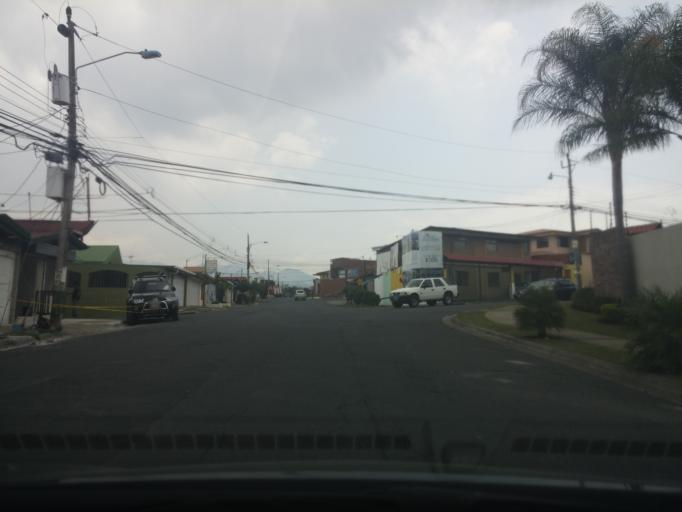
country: CR
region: Heredia
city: San Pablo
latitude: 9.9883
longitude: -84.1069
